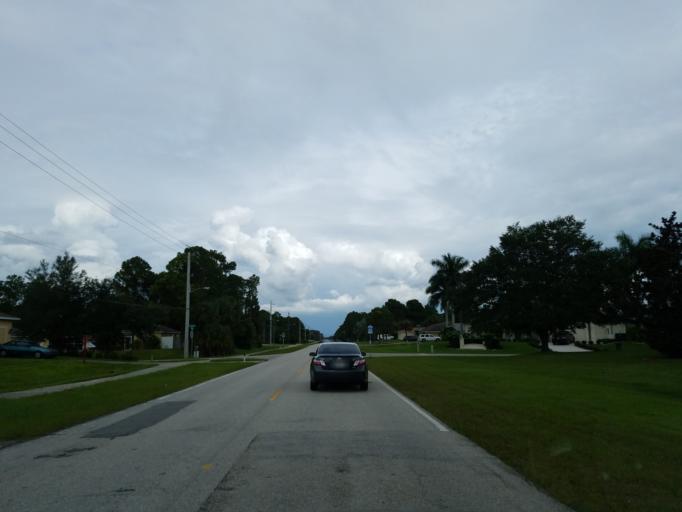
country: US
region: Florida
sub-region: Sarasota County
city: North Port
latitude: 27.0687
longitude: -82.1794
